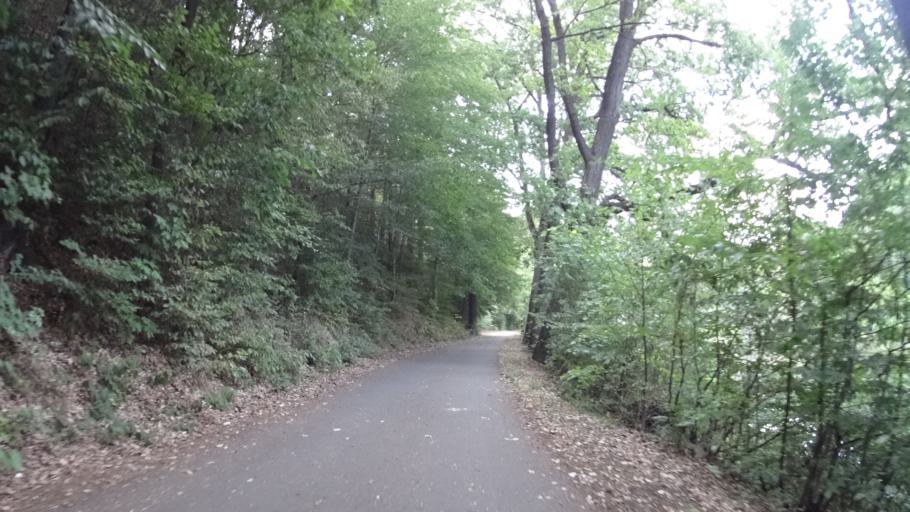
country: DE
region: Saxony
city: Ostritz
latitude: 50.9953
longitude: 14.9169
